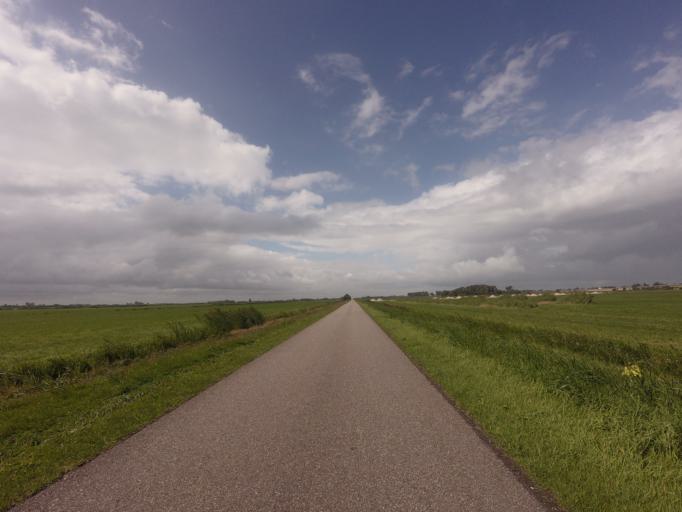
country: NL
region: Friesland
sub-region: Gemeente Skarsterlan
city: Sint Nicolaasga
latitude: 52.9744
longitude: 5.7441
